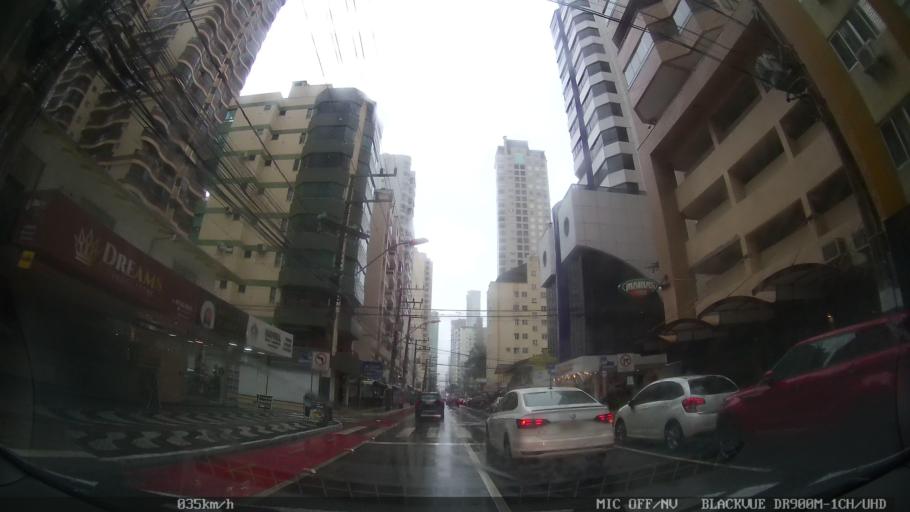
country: BR
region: Santa Catarina
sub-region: Balneario Camboriu
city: Balneario Camboriu
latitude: -26.9963
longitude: -48.6279
